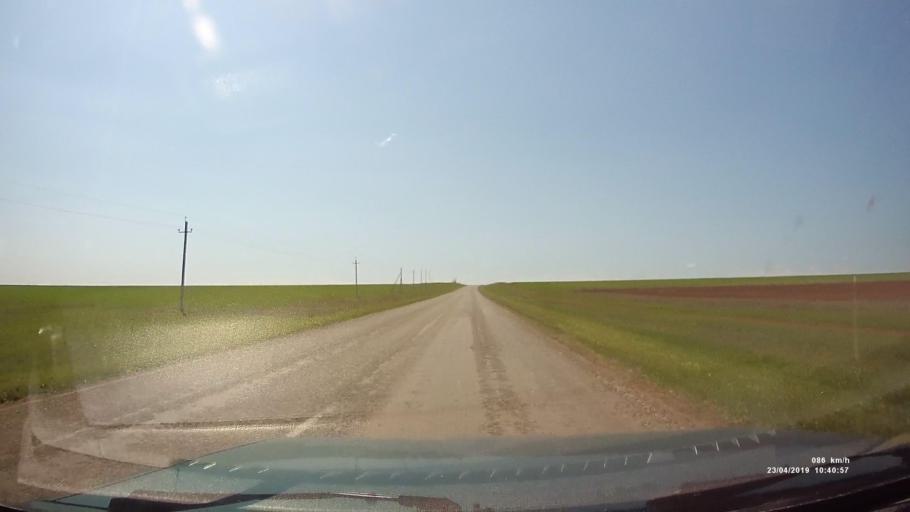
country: RU
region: Kalmykiya
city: Yashalta
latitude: 46.4997
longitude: 42.6384
